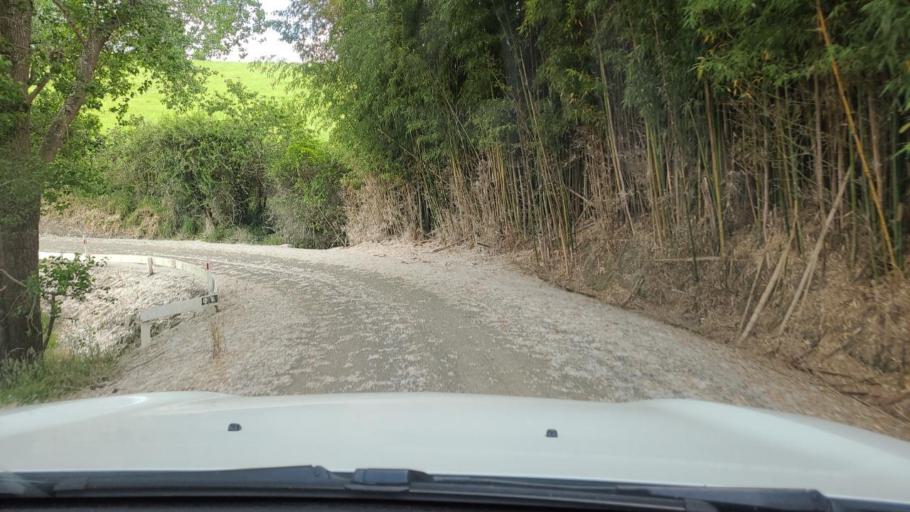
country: NZ
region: Waikato
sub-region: Matamata-Piako District
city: Matamata
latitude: -37.8008
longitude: 175.6311
